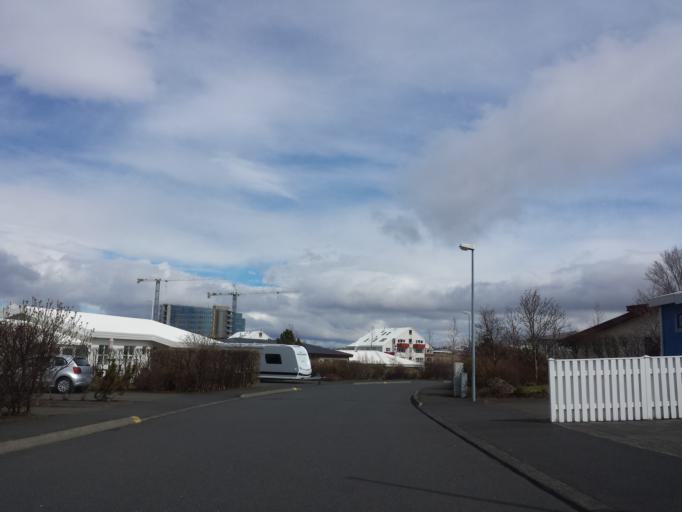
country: IS
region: Capital Region
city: Kopavogur
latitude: 64.1001
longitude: -21.8945
